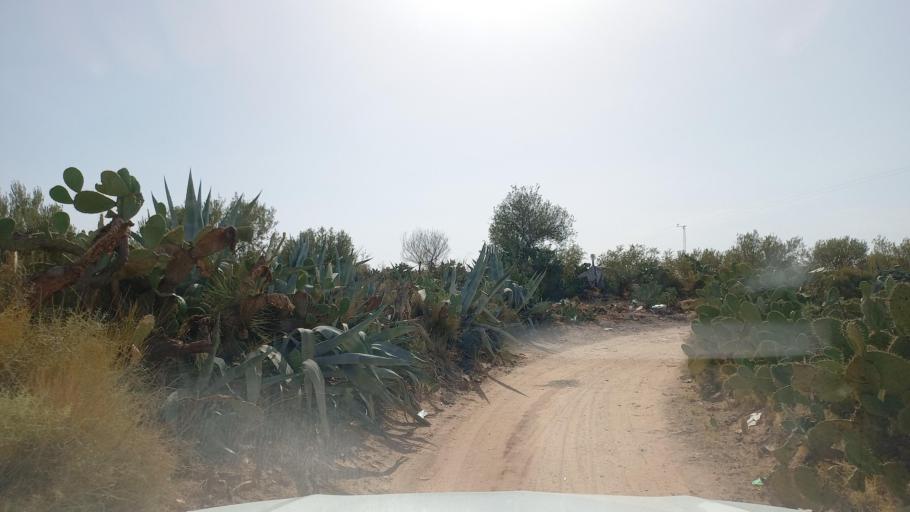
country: TN
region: Al Qasrayn
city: Kasserine
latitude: 35.2097
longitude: 8.9825
